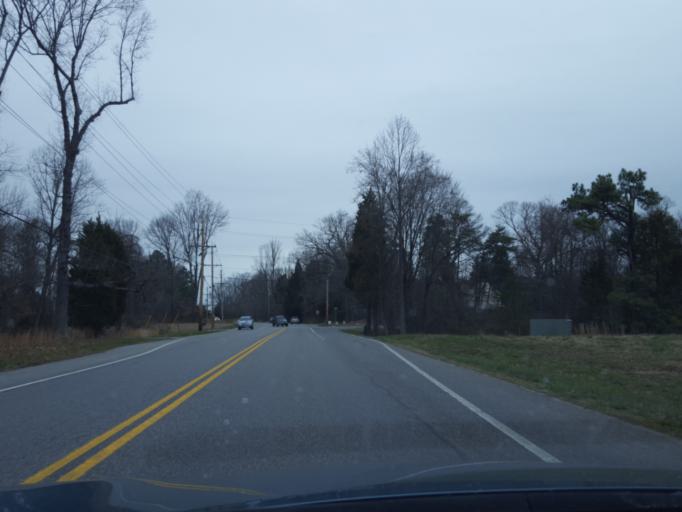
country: US
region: Maryland
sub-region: Calvert County
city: Prince Frederick
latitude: 38.4731
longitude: -76.5472
